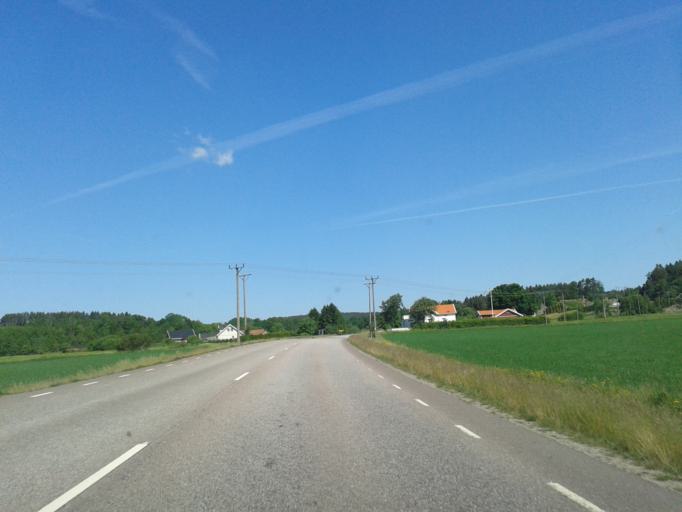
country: SE
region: Vaestra Goetaland
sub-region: Kungalvs Kommun
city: Kungalv
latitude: 57.9096
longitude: 11.9203
